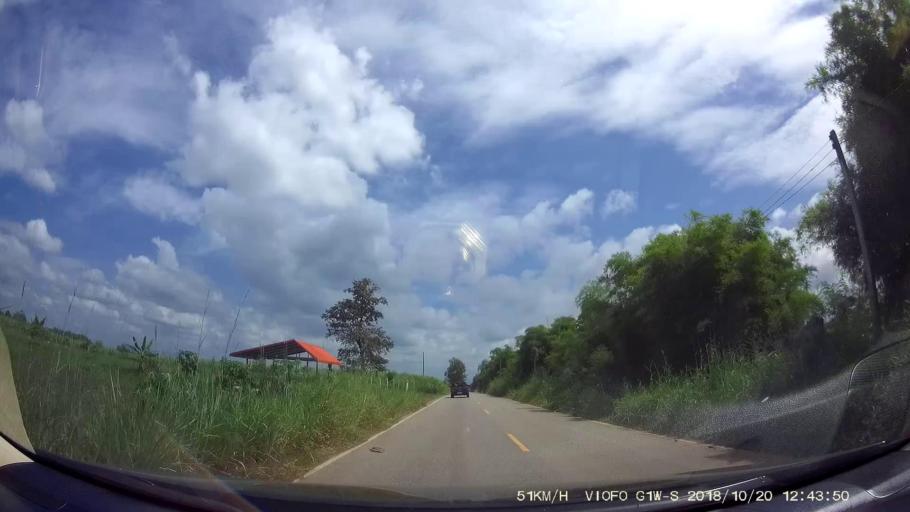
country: TH
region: Chaiyaphum
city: Khon San
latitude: 16.5408
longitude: 101.8641
